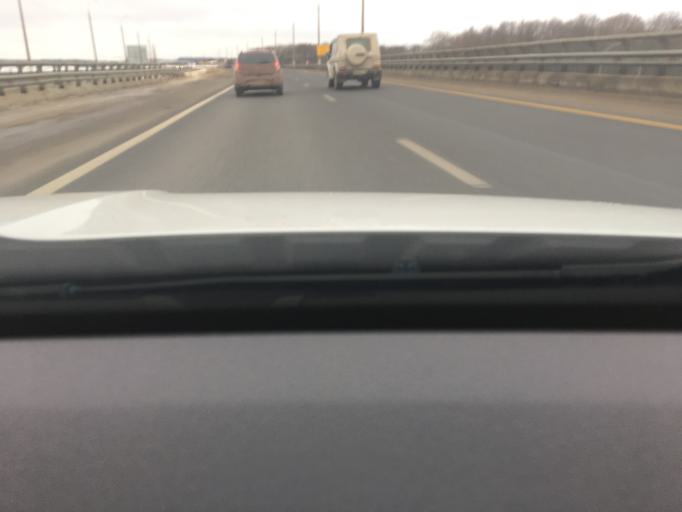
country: RU
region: Moskovskaya
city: Serpukhov
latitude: 54.8334
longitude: 37.4620
